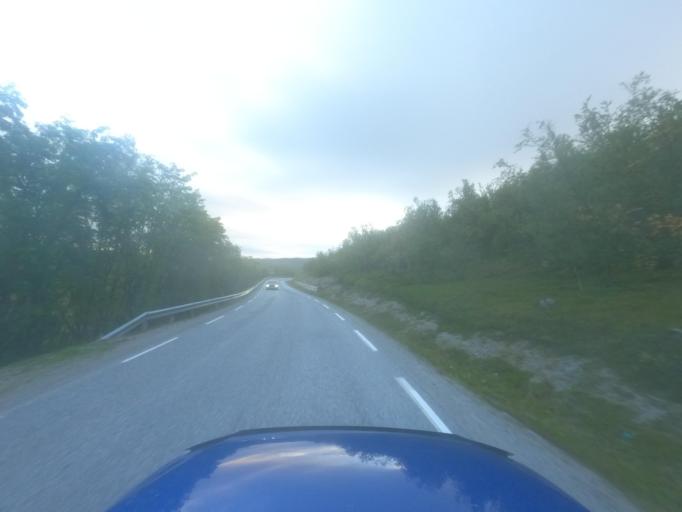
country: NO
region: Finnmark Fylke
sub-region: Porsanger
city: Lakselv
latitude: 70.3666
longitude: 25.0747
